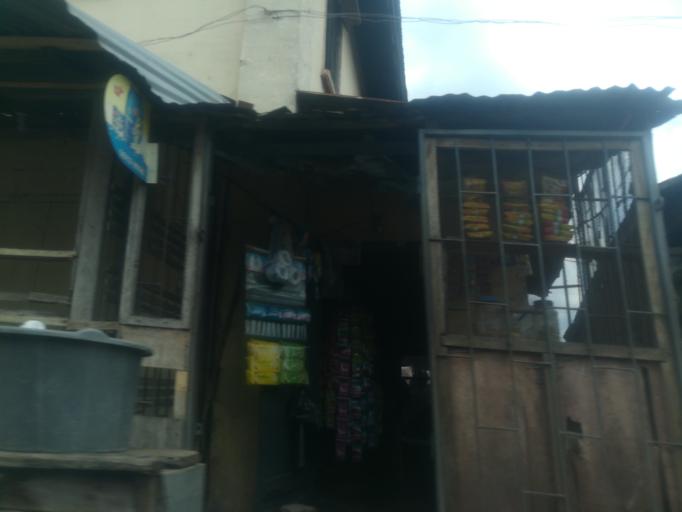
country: NG
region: Oyo
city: Ibadan
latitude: 7.3947
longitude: 3.8833
